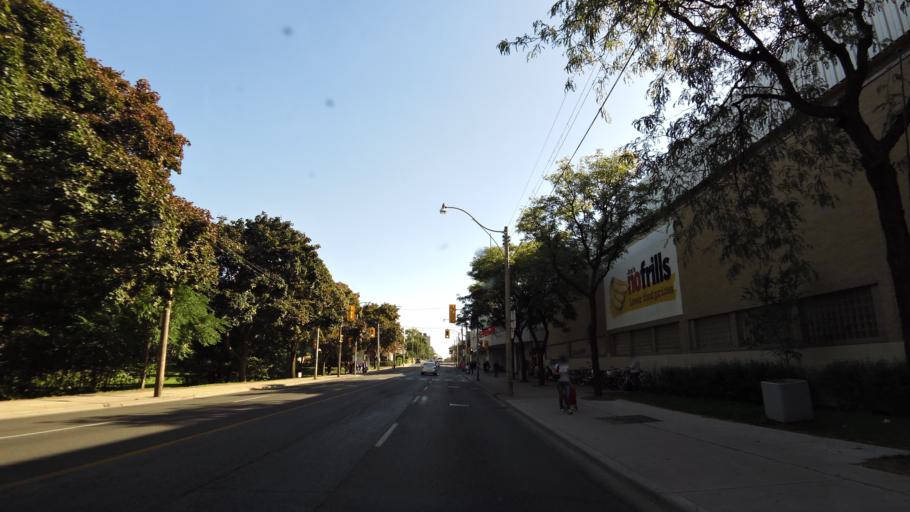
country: CA
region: Ontario
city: Toronto
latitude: 43.6557
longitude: -79.4338
